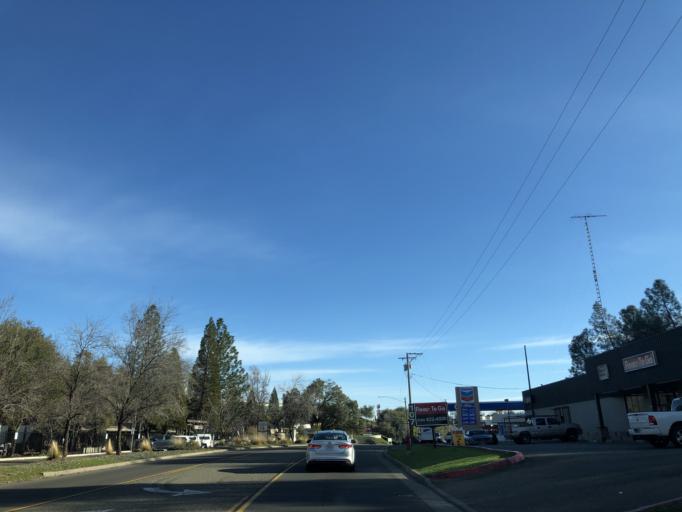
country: US
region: California
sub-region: El Dorado County
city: Diamond Springs
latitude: 38.7251
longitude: -120.8353
